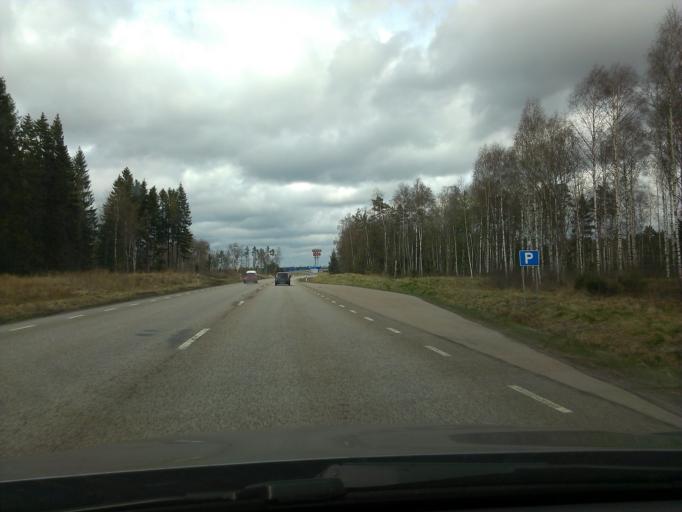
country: SE
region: Kronoberg
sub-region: Almhults Kommun
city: AElmhult
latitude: 56.5425
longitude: 14.1526
